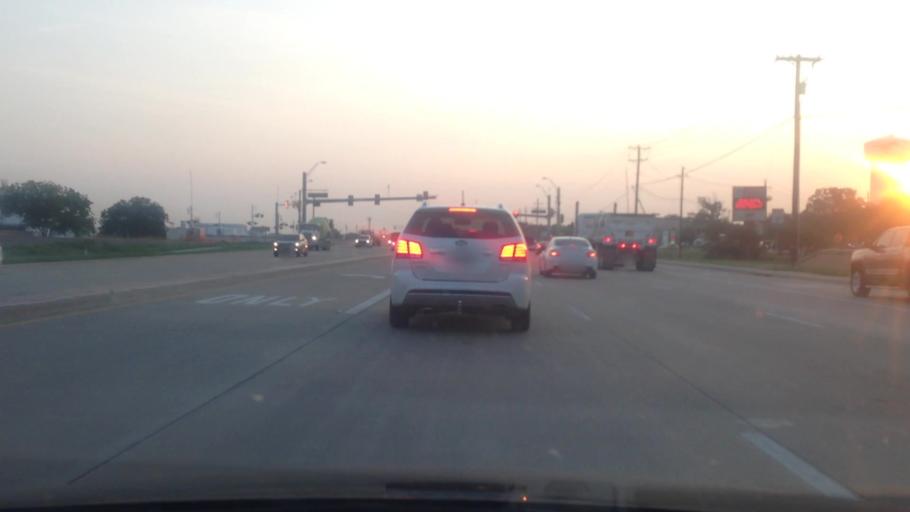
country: US
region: Texas
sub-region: Tarrant County
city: Southlake
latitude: 32.9183
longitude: -97.1205
